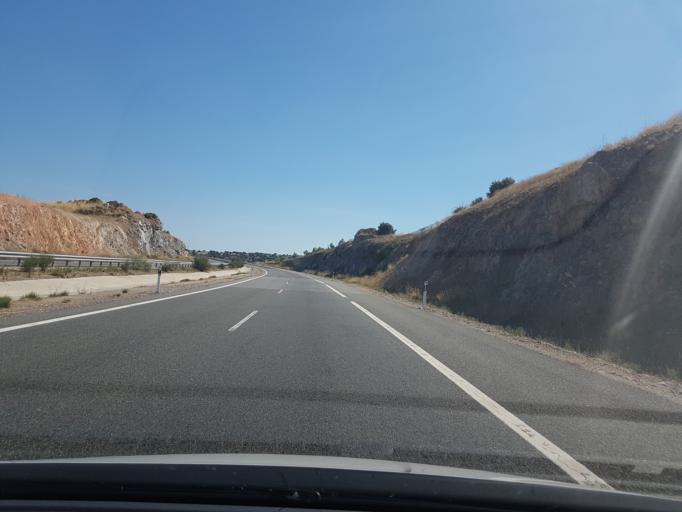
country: ES
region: Castille and Leon
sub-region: Provincia de Avila
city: Cardenosa
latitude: 40.7394
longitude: -4.7572
